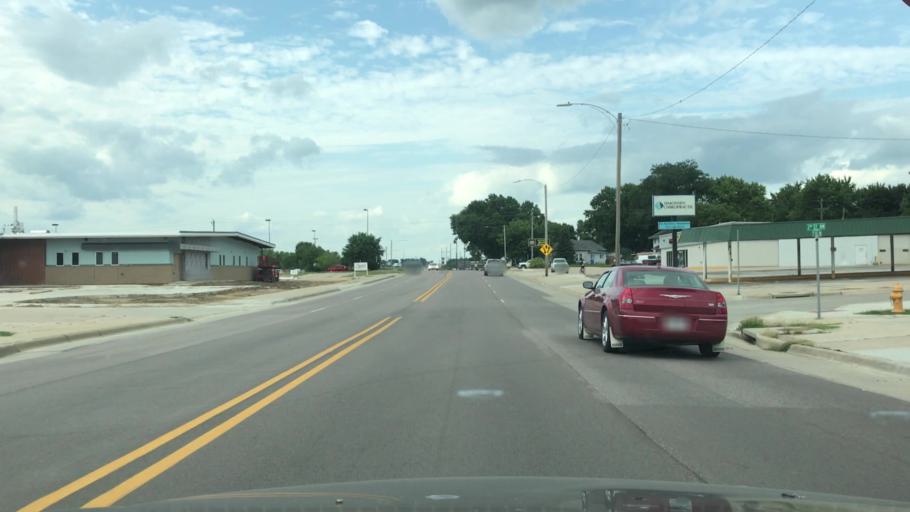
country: US
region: Iowa
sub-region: Plymouth County
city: Le Mars
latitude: 42.7953
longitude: -96.1738
